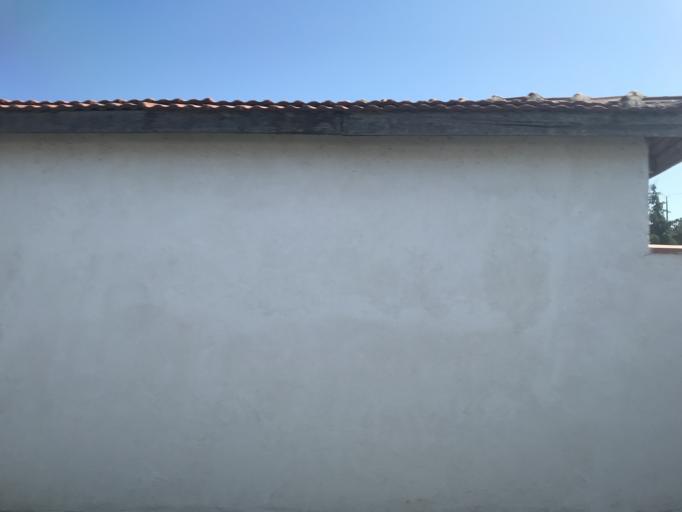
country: TR
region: Kirklareli
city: Kirklareli
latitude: 41.7744
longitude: 27.2267
